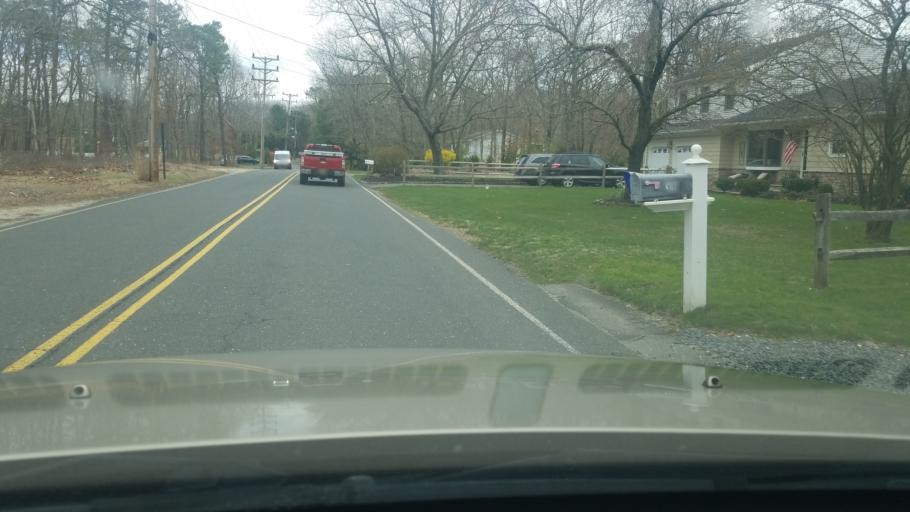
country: US
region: New Jersey
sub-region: Monmouth County
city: Ramtown
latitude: 40.1374
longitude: -74.1429
